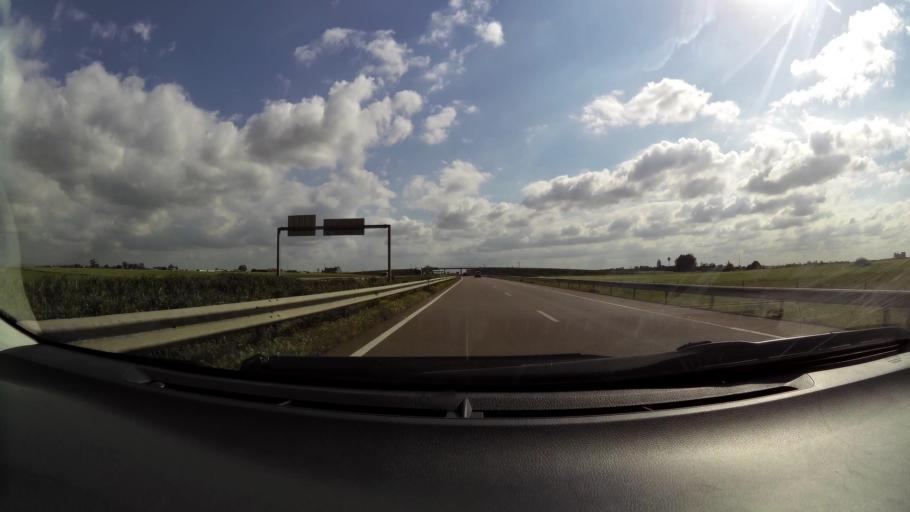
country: MA
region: Chaouia-Ouardigha
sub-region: Settat Province
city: Berrechid
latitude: 33.2404
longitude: -7.5686
